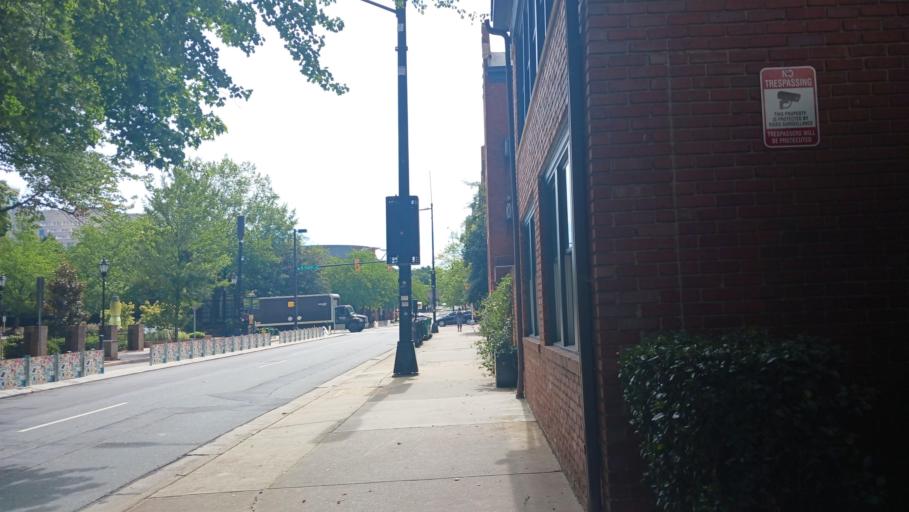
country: US
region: North Carolina
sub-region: Mecklenburg County
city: Charlotte
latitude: 35.2310
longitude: -80.8435
